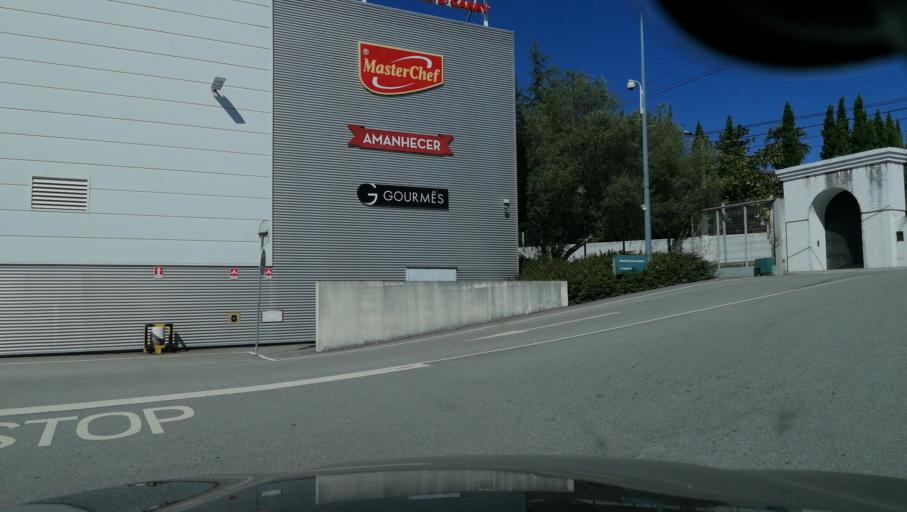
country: PT
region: Aveiro
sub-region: Santa Maria da Feira
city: Feira
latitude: 40.9317
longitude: -8.5265
